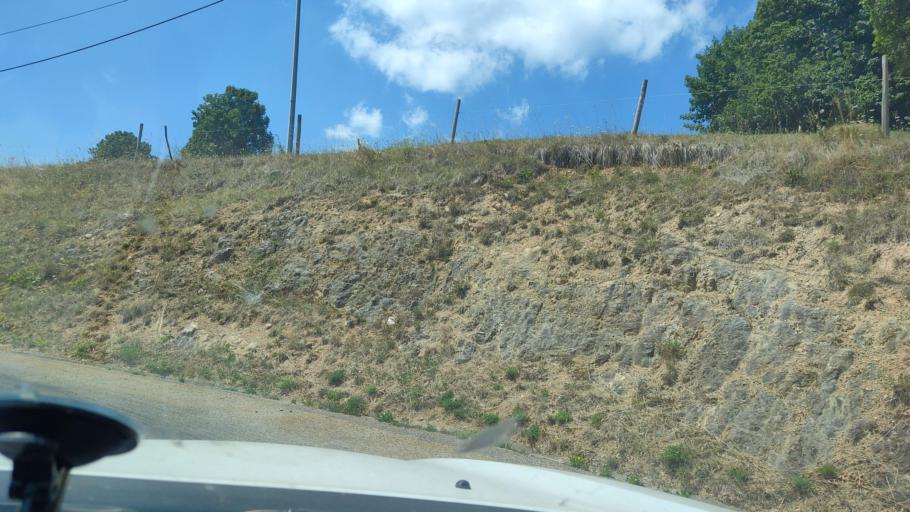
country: FR
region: Rhone-Alpes
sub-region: Departement de la Haute-Savoie
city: Cusy
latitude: 45.6713
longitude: 6.0404
